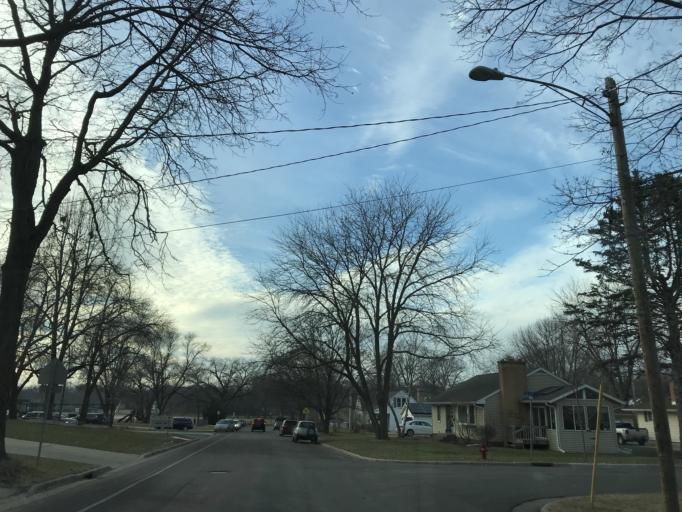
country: US
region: Wisconsin
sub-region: Dane County
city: Monona
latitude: 43.0659
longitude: -89.3370
